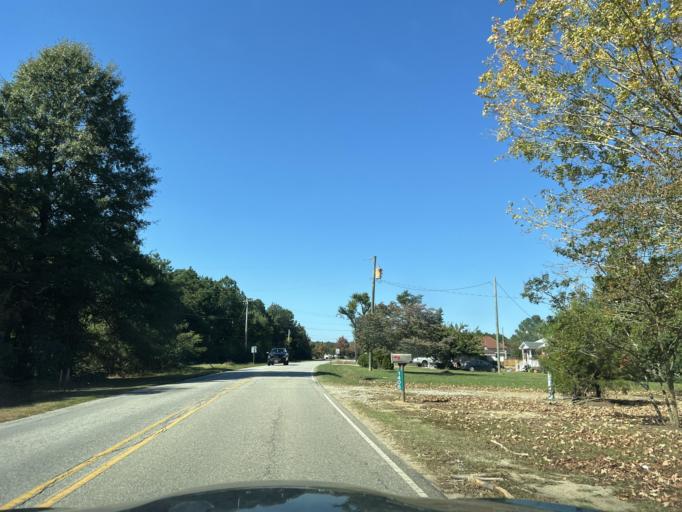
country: US
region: North Carolina
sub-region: Johnston County
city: Clayton
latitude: 35.6666
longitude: -78.4741
